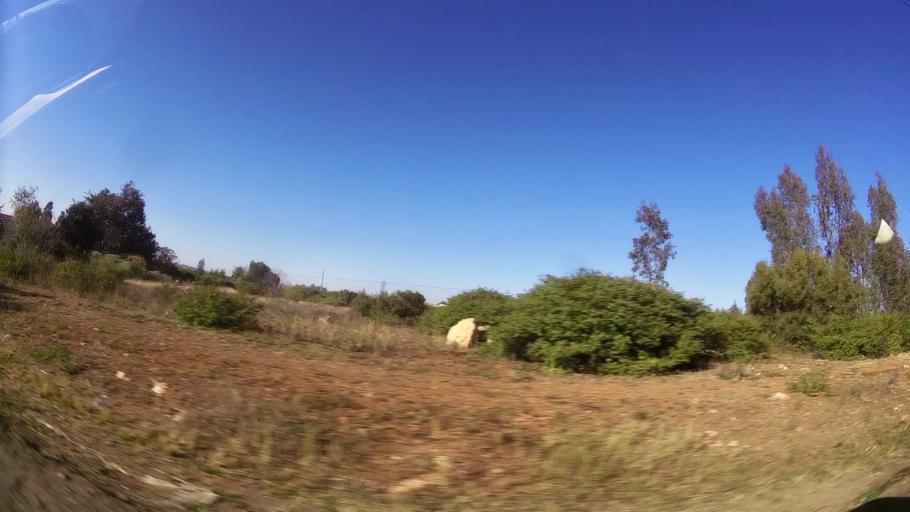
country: ZA
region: Gauteng
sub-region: City of Tshwane Metropolitan Municipality
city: Centurion
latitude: -25.8147
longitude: 28.2287
